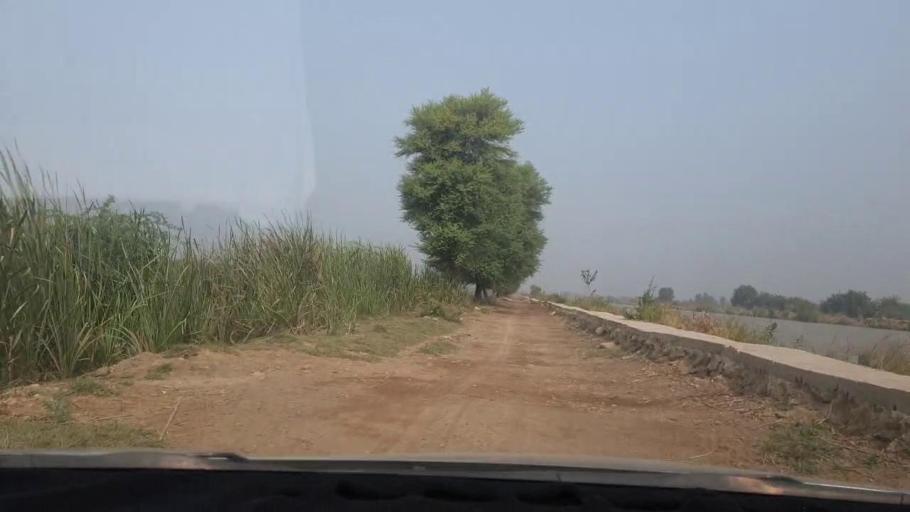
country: PK
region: Sindh
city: Matiari
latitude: 25.6606
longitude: 68.5602
